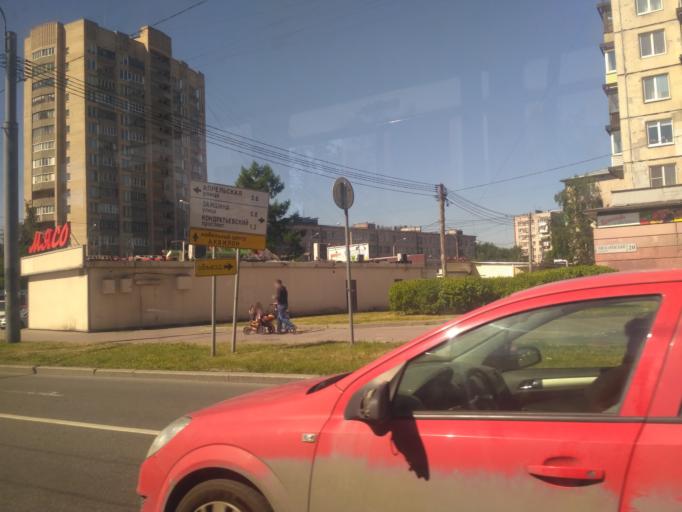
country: RU
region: Leningrad
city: Kalininskiy
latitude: 59.9692
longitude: 30.4109
